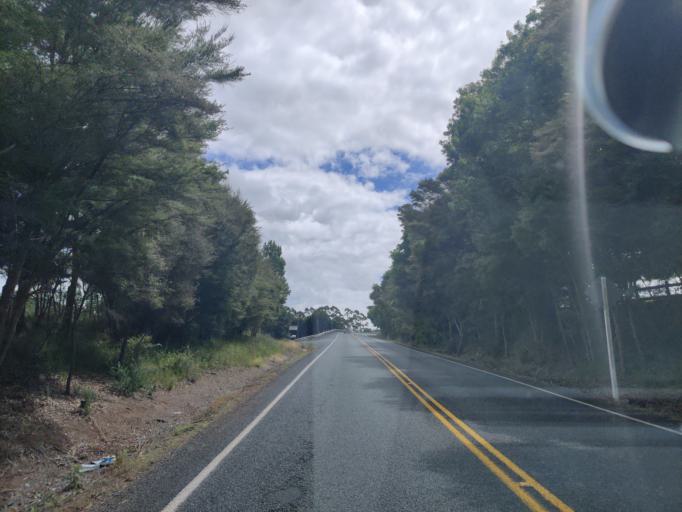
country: NZ
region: Northland
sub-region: Far North District
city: Paihia
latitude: -35.2911
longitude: 174.0115
